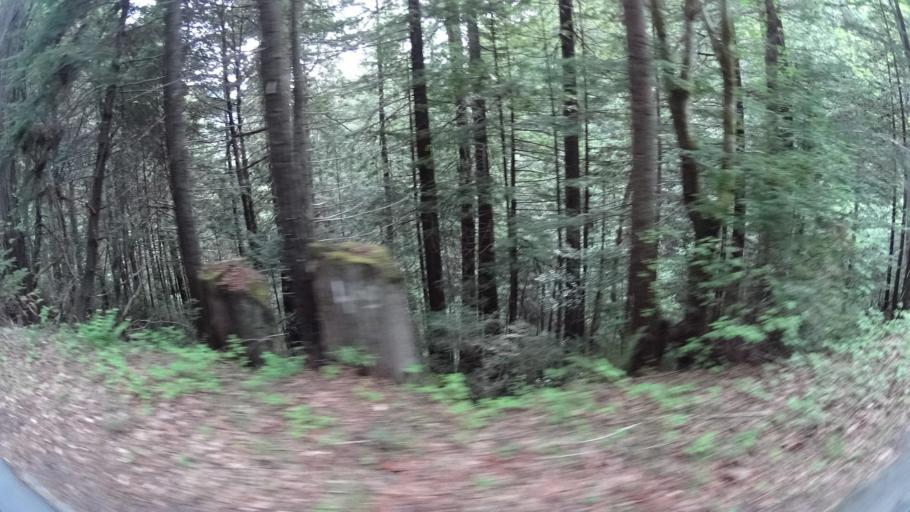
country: US
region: California
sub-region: Humboldt County
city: Redway
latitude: 40.3381
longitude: -123.8672
